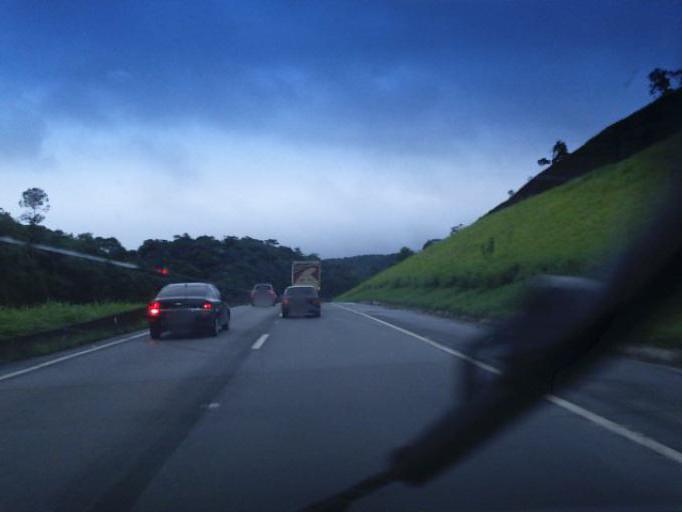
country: BR
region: Sao Paulo
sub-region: Miracatu
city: Miracatu
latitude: -24.1906
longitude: -47.3597
